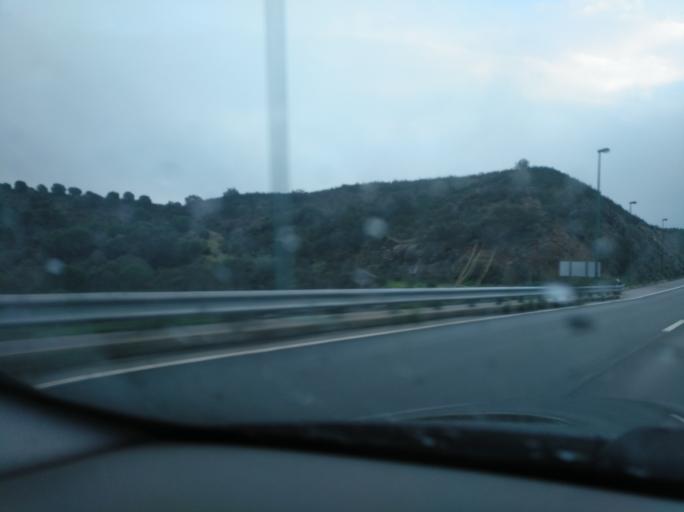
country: PT
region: Faro
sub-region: Castro Marim
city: Castro Marim
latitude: 37.3259
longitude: -7.4864
